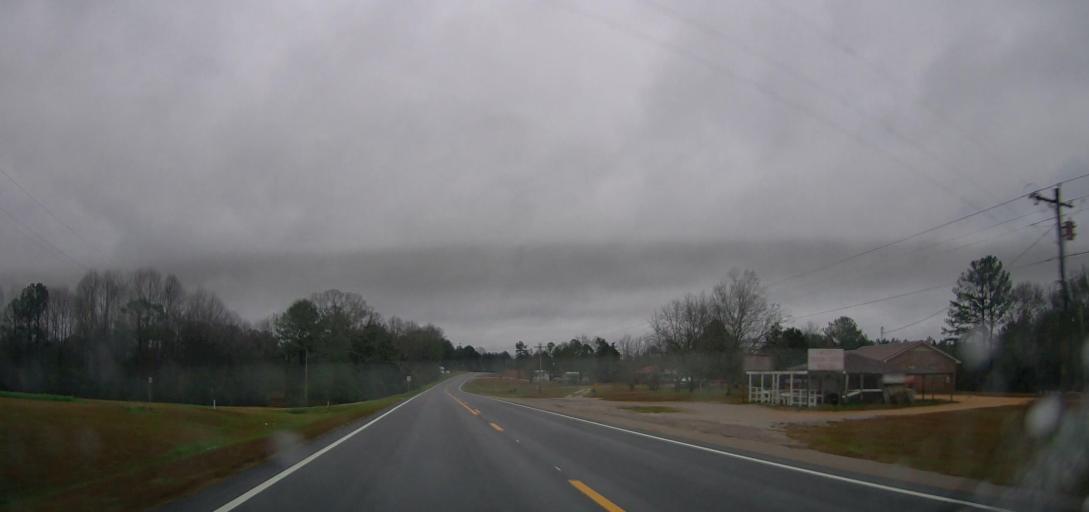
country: US
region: Alabama
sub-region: Chilton County
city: Thorsby
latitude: 32.8013
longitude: -86.9142
